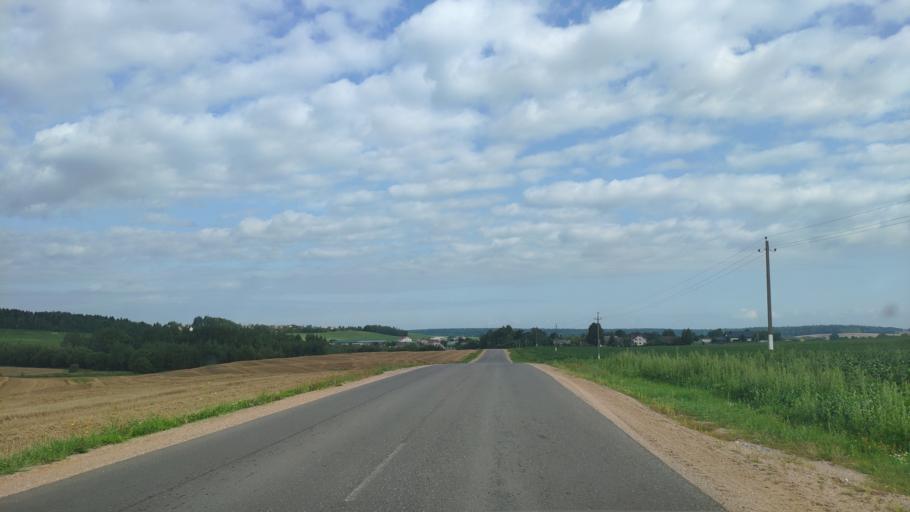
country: BY
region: Minsk
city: Khatsyezhyna
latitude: 53.8464
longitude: 27.3131
